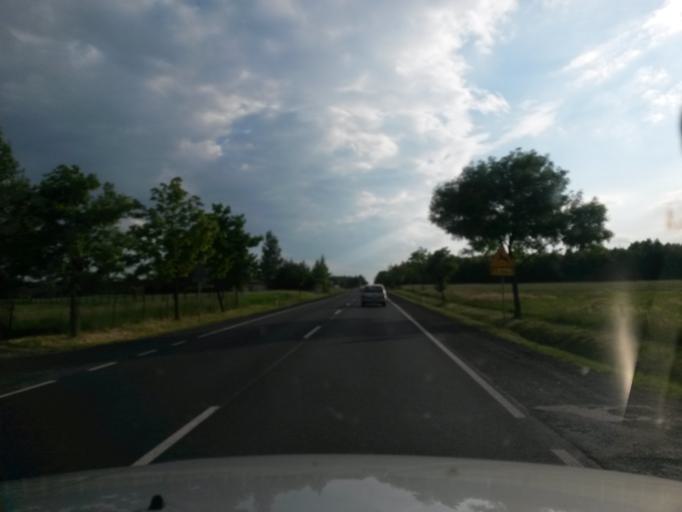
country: PL
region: Lodz Voivodeship
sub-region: Powiat belchatowski
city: Druzbice
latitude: 51.4071
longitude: 19.4506
